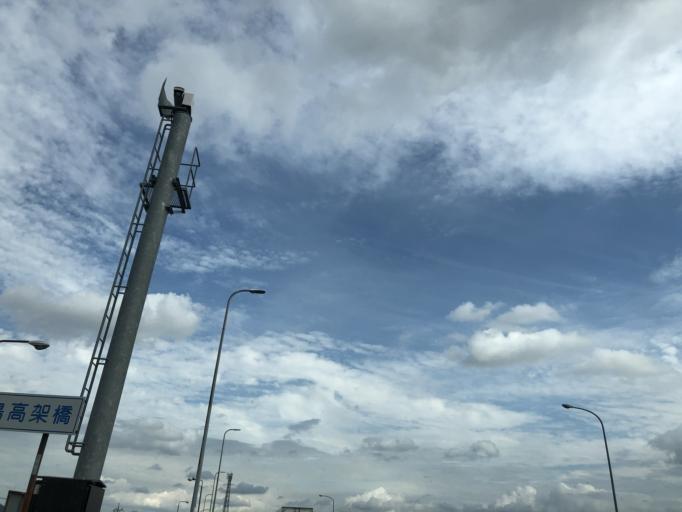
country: JP
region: Tochigi
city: Sano
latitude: 36.2880
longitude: 139.5629
